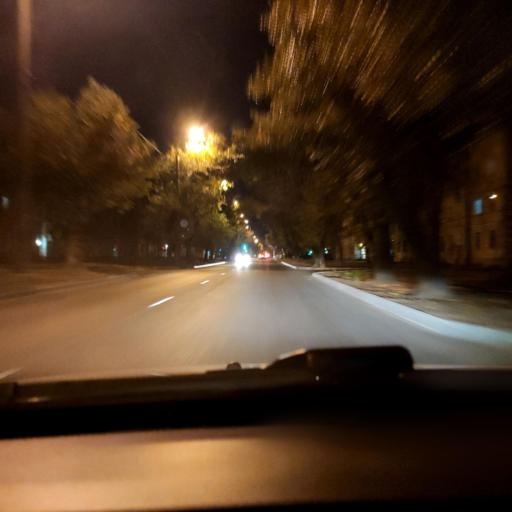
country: RU
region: Voronezj
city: Voronezh
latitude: 51.6403
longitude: 39.2400
